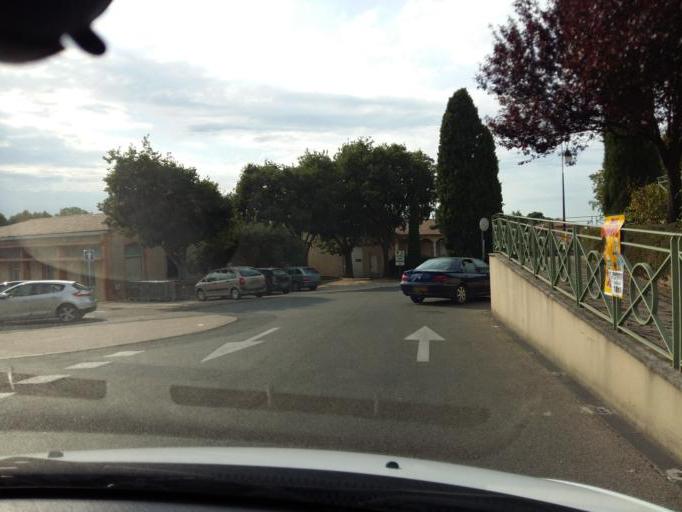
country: FR
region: Provence-Alpes-Cote d'Azur
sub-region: Departement du Vaucluse
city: Saint-Didier
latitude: 44.0057
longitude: 5.1116
